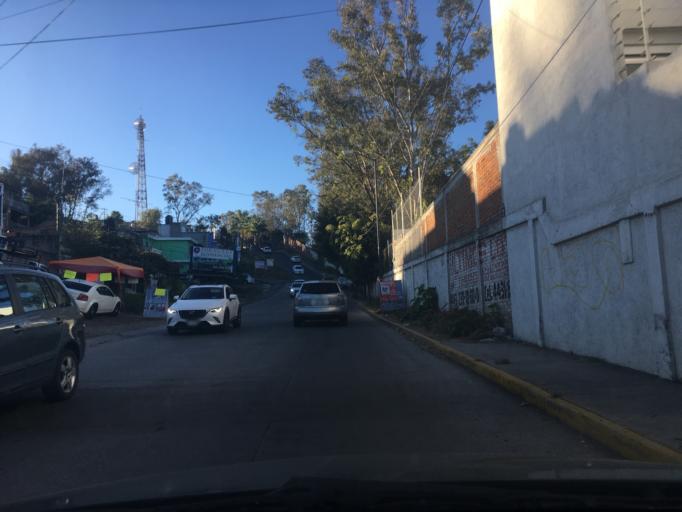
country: MX
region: Michoacan
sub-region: Morelia
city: Montana Monarca (Punta Altozano)
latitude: 19.6673
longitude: -101.2013
